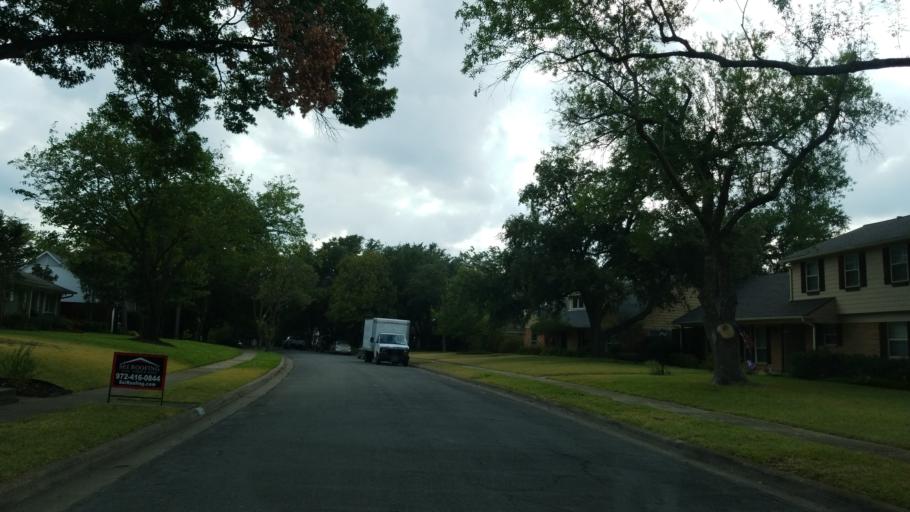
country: US
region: Texas
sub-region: Dallas County
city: Richardson
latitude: 32.9322
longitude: -96.7787
